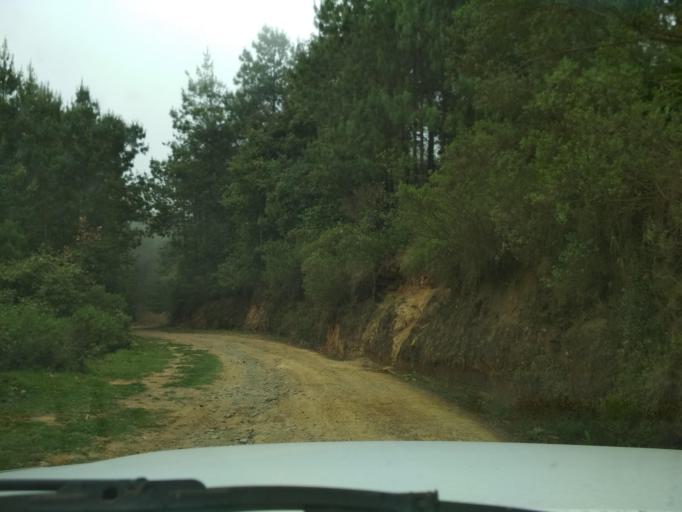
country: MX
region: Veracruz
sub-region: Mariano Escobedo
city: Loma Grande
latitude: 18.9302
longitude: -97.2193
